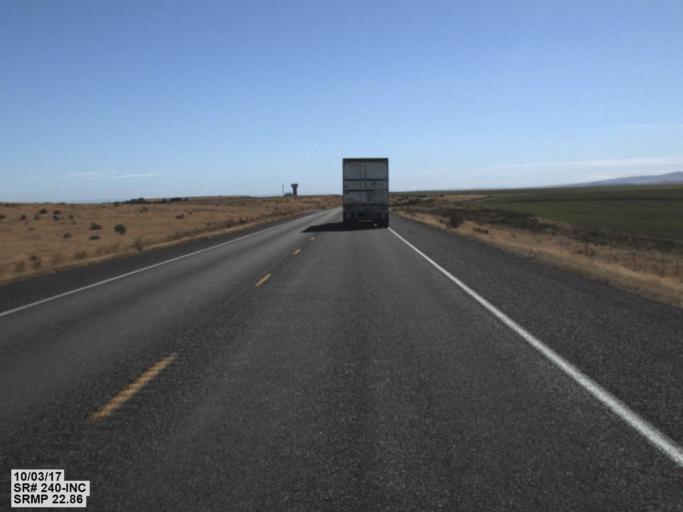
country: US
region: Washington
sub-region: Benton County
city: West Richland
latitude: 46.3619
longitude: -119.3836
